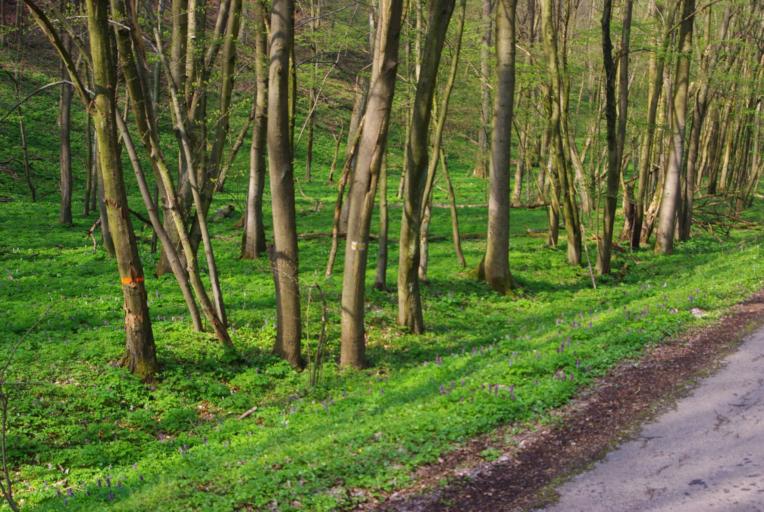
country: HU
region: Fejer
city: Szarliget
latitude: 47.4618
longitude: 18.4504
